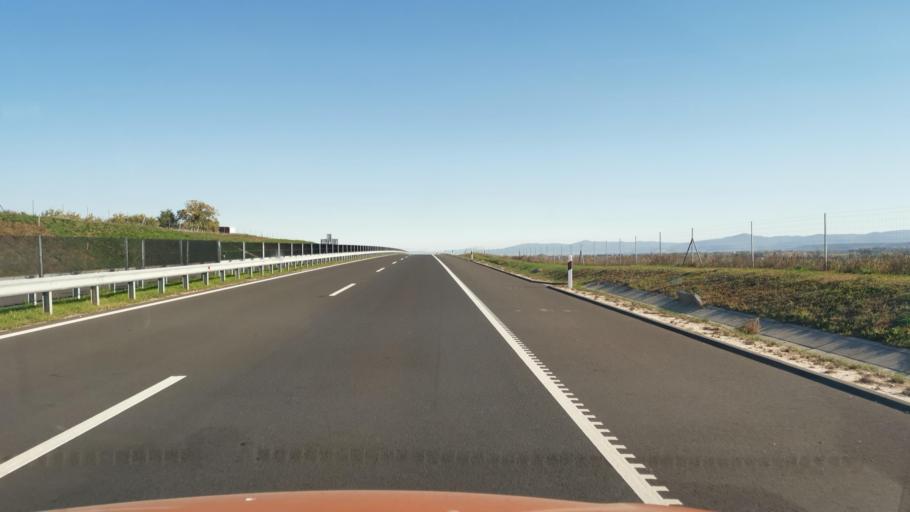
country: HU
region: Borsod-Abauj-Zemplen
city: Halmaj
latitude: 48.2588
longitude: 20.9850
